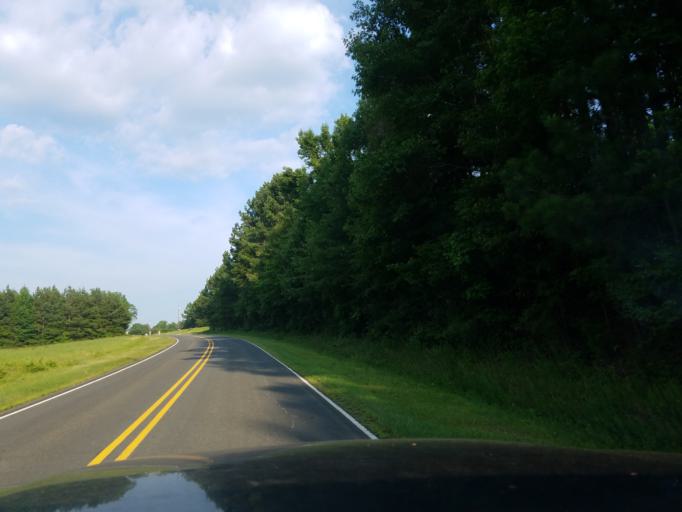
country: US
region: North Carolina
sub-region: Granville County
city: Butner
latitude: 36.1956
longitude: -78.8376
